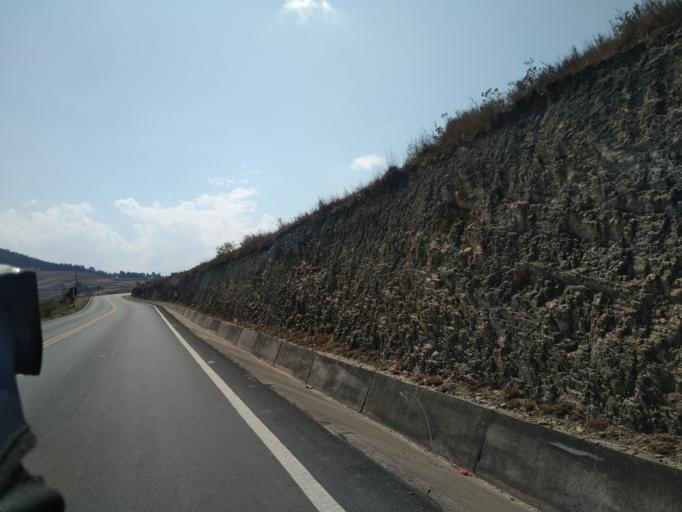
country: PE
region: Cajamarca
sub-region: Provincia de Cajamarca
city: Llacanora
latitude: -7.2068
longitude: -78.3897
